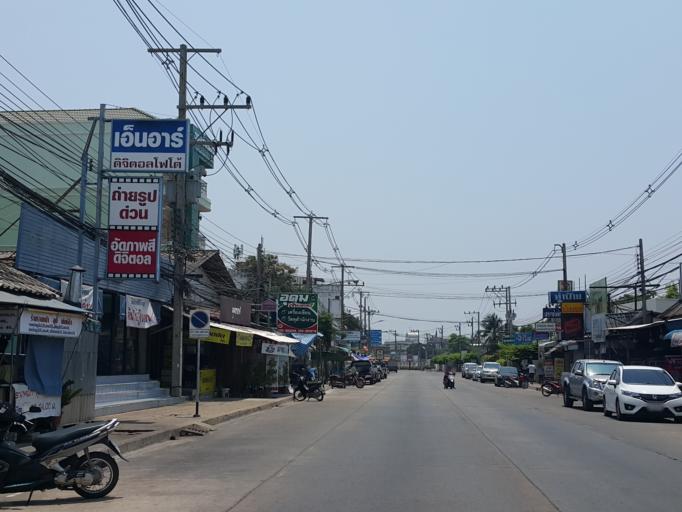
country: TH
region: Phitsanulok
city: Phitsanulok
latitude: 16.8158
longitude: 100.2574
